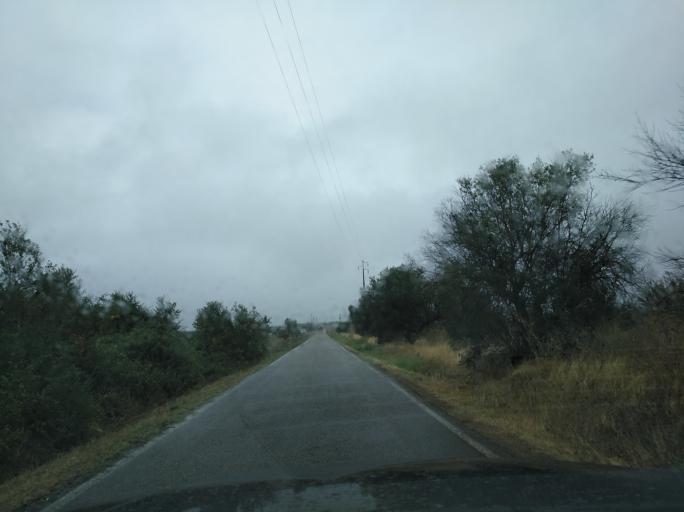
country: PT
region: Portalegre
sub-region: Campo Maior
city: Campo Maior
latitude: 38.9524
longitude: -7.0856
